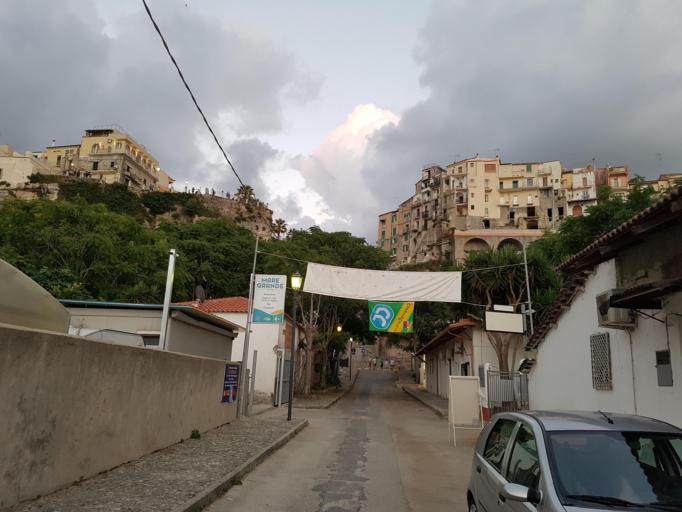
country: IT
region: Calabria
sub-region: Provincia di Vibo-Valentia
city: Tropea
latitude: 38.6789
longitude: 15.8944
